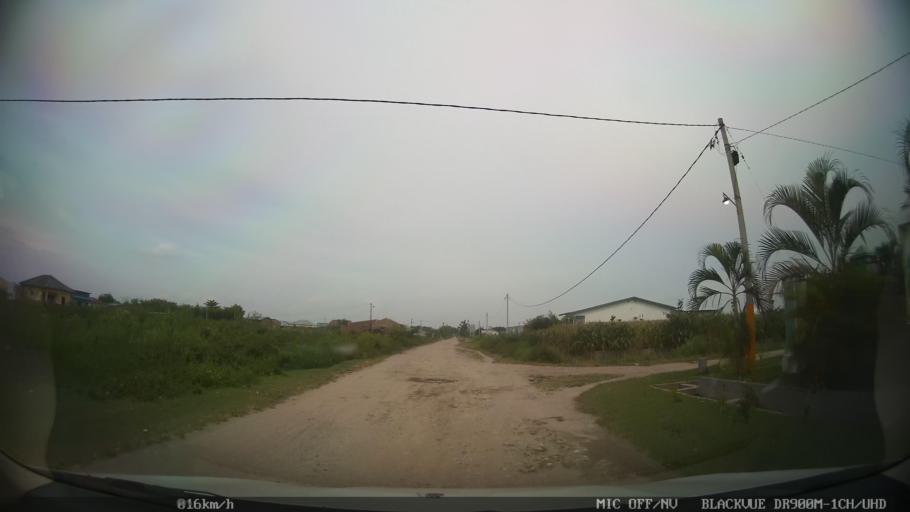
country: ID
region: North Sumatra
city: Medan
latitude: 3.5733
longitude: 98.7506
